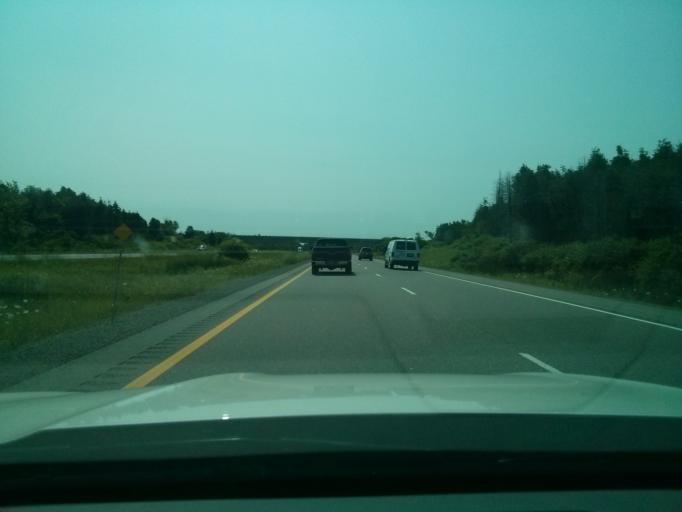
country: CA
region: Ontario
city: Bells Corners
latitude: 45.0957
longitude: -75.6547
